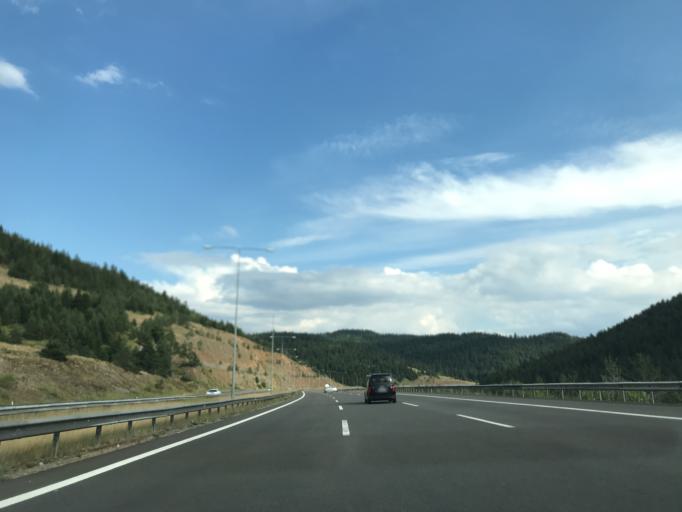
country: TR
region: Ankara
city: Pecenek
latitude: 40.6007
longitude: 32.2800
